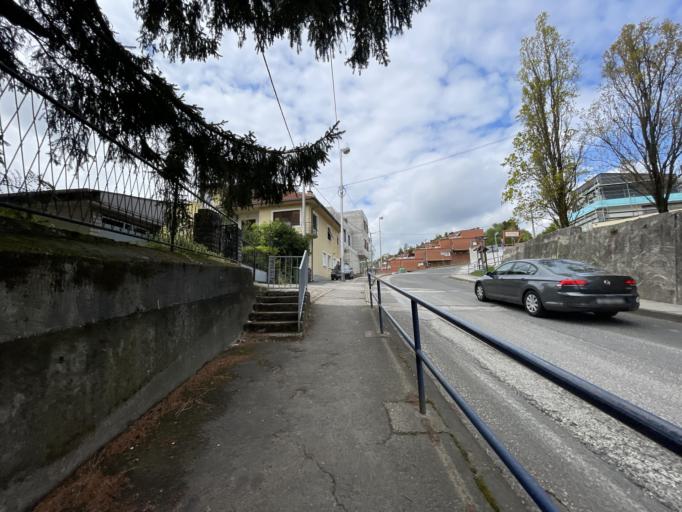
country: HR
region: Grad Zagreb
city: Zagreb - Centar
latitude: 45.8164
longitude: 15.9426
